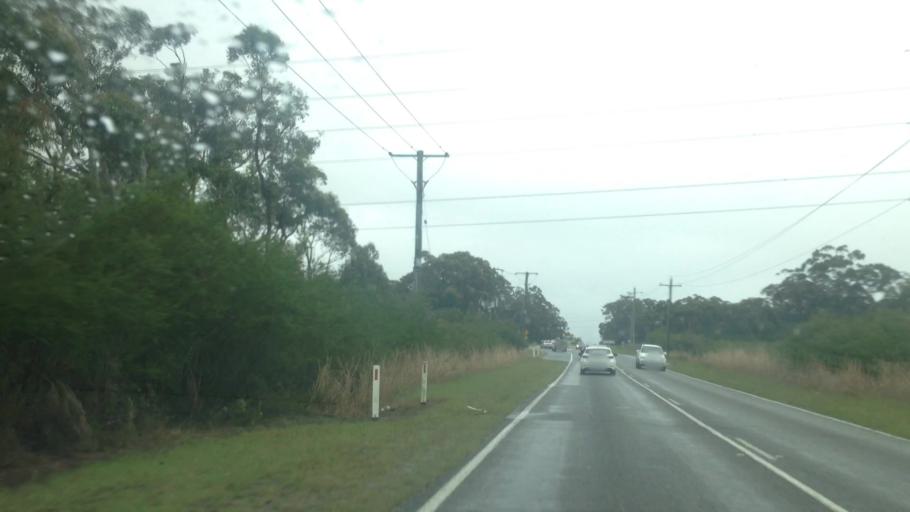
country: AU
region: New South Wales
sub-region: Wyong Shire
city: Charmhaven
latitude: -33.1586
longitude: 151.4786
